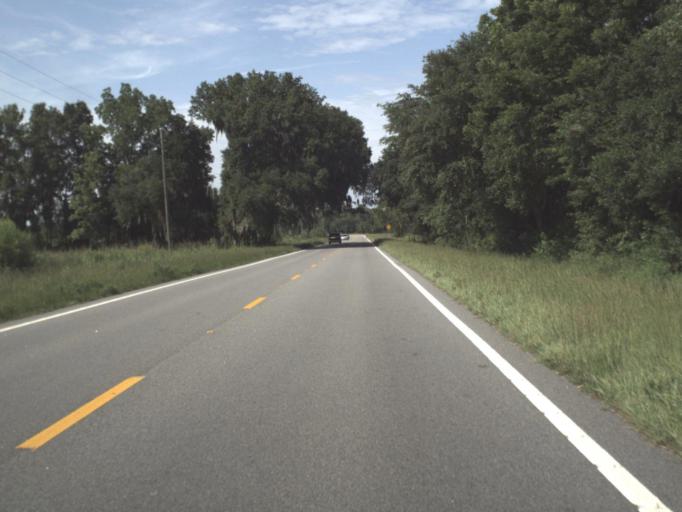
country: US
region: Florida
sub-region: Madison County
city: Madison
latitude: 30.5612
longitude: -83.3646
